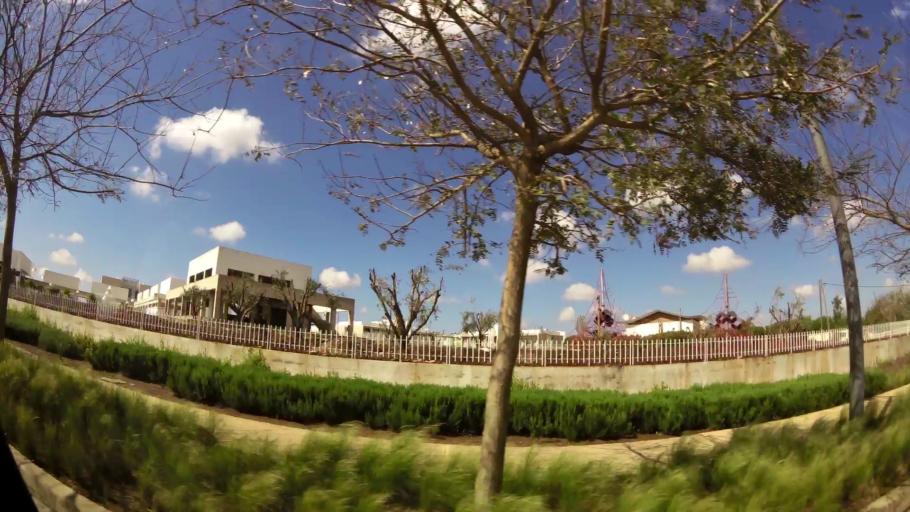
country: MA
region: Grand Casablanca
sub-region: Nouaceur
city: Bouskoura
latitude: 33.4933
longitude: -7.6017
